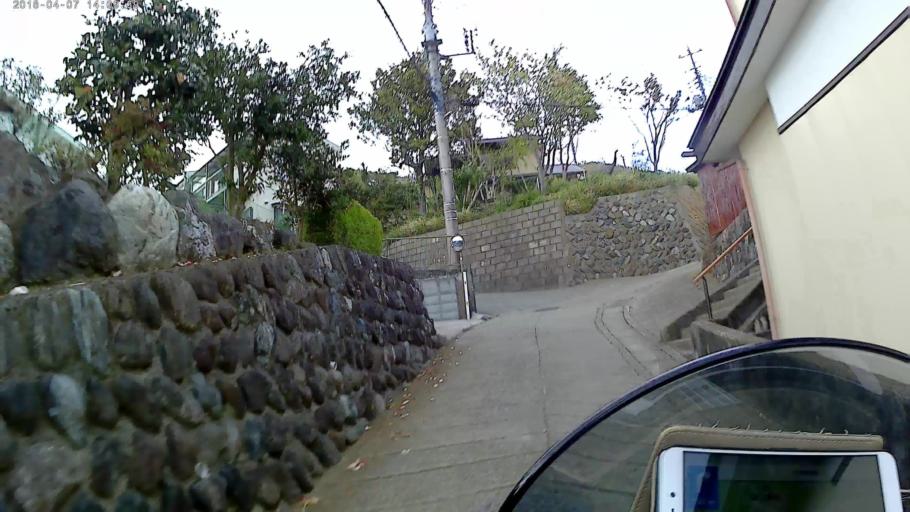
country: JP
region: Kanagawa
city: Hadano
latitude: 35.3678
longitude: 139.2442
